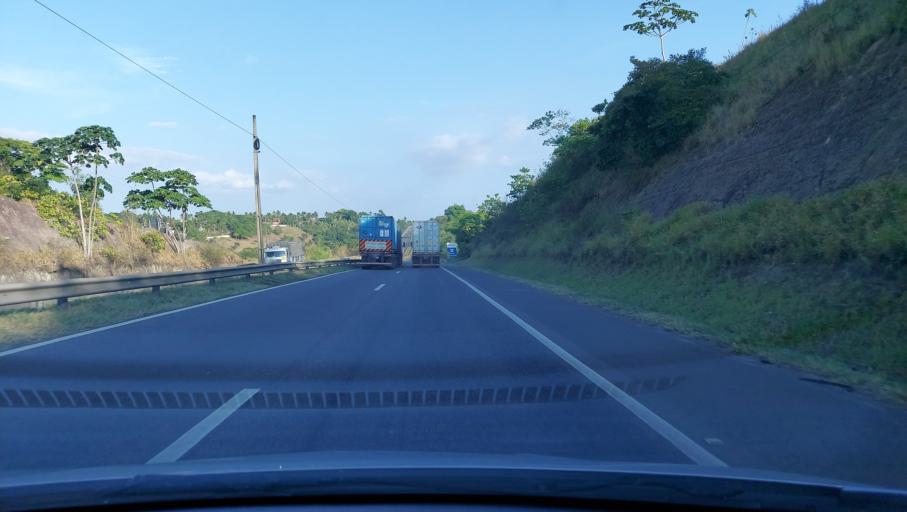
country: BR
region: Bahia
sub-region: Conceicao Do Jacuipe
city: Conceicao do Jacuipe
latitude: -12.3940
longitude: -38.7757
